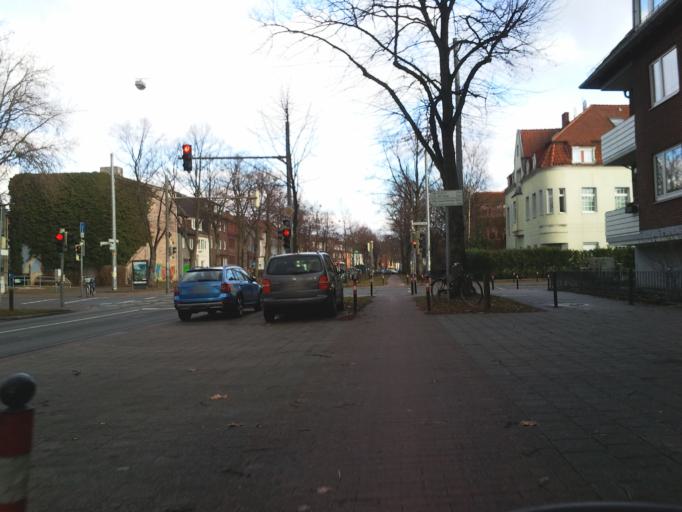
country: DE
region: Bremen
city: Bremen
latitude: 53.0992
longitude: 8.7774
